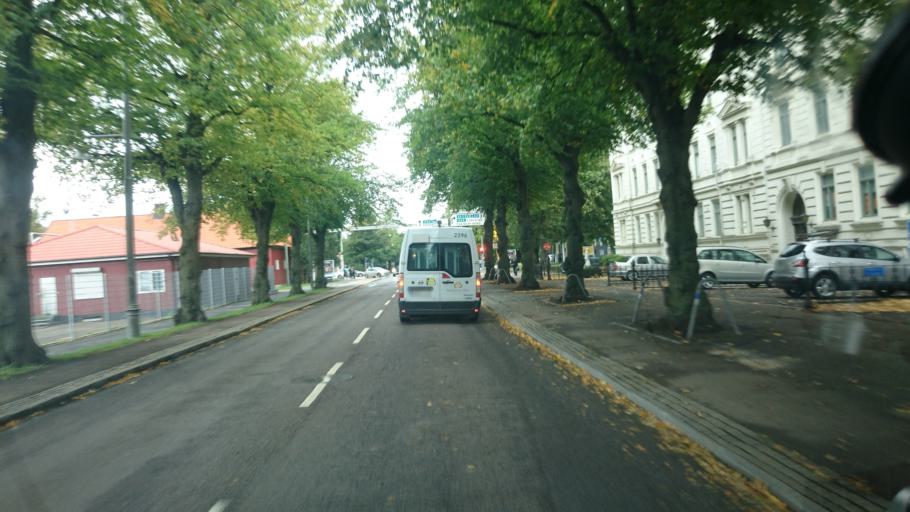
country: SE
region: Vaestra Goetaland
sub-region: Goteborg
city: Goeteborg
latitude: 57.7034
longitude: 11.9798
